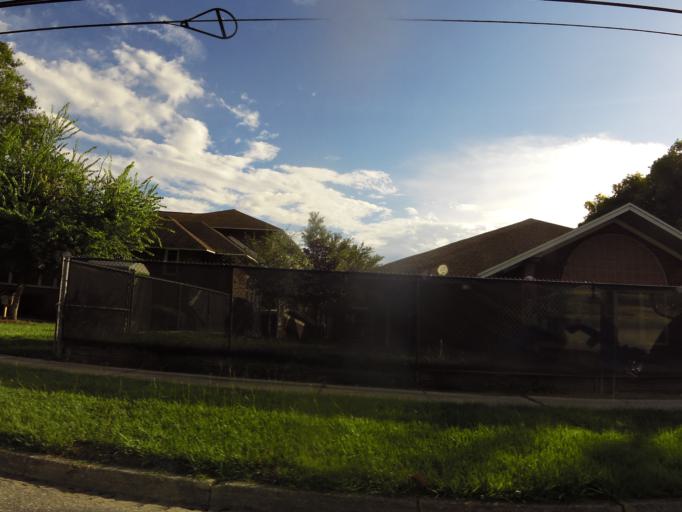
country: US
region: Florida
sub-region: Duval County
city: Jacksonville
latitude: 30.3077
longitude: -81.7198
